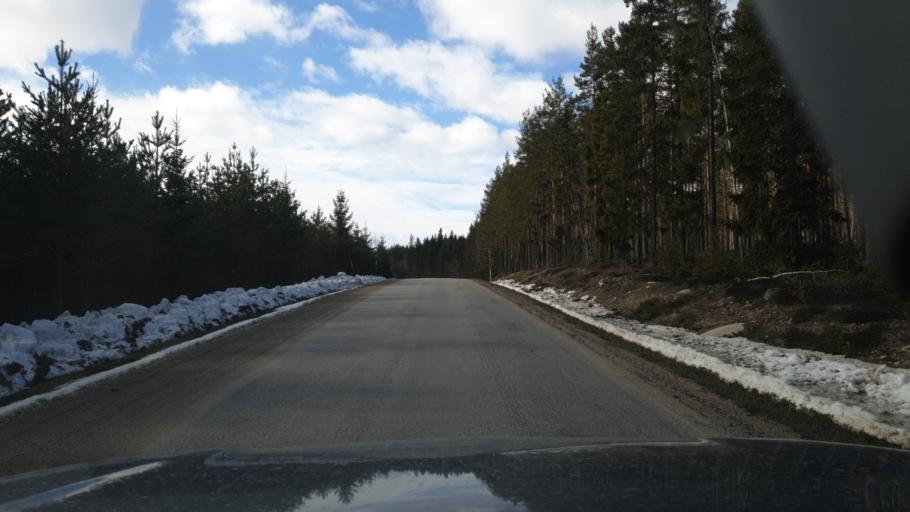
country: SE
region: Gaevleborg
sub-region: Ljusdals Kommun
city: Ljusdal
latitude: 61.8467
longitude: 15.9672
